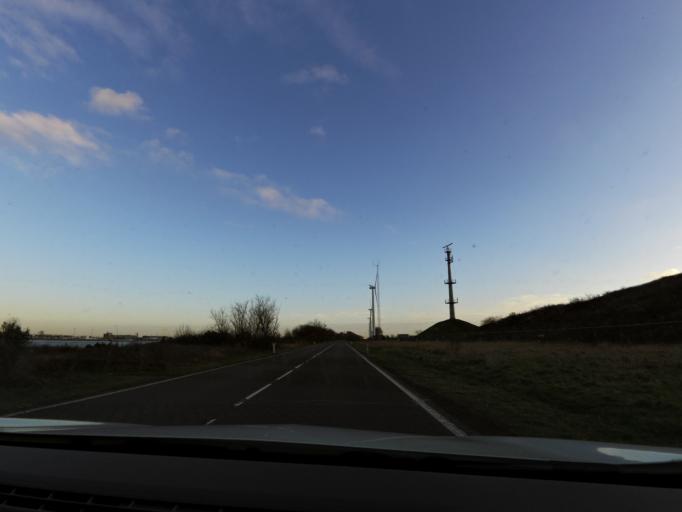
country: NL
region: South Holland
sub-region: Gemeente Rotterdam
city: Hoek van Holland
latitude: 51.9659
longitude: 4.1323
